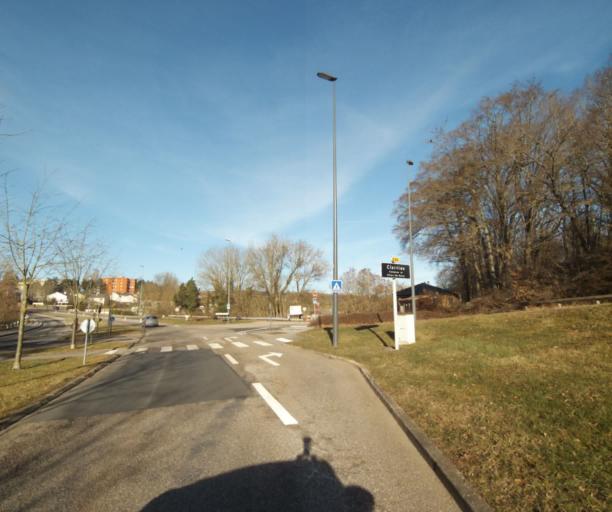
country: FR
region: Lorraine
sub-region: Departement de Meurthe-et-Moselle
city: Chavigny
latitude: 48.6586
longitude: 6.1181
